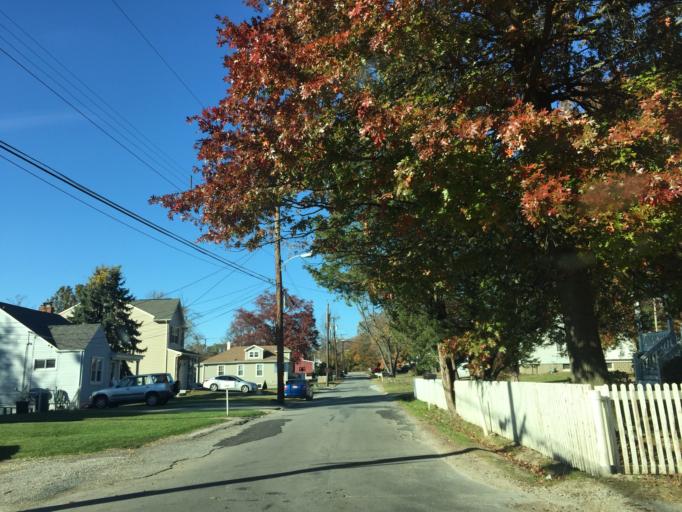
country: US
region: Maryland
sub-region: Baltimore County
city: Parkville
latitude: 39.3971
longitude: -76.5530
